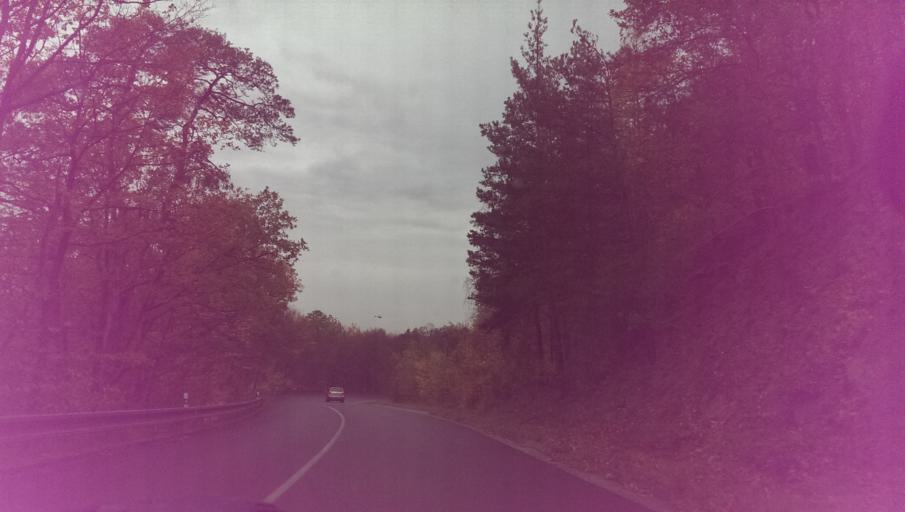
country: AT
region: Lower Austria
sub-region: Politischer Bezirk Hollabrunn
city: Hardegg
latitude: 48.8953
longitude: 15.8215
